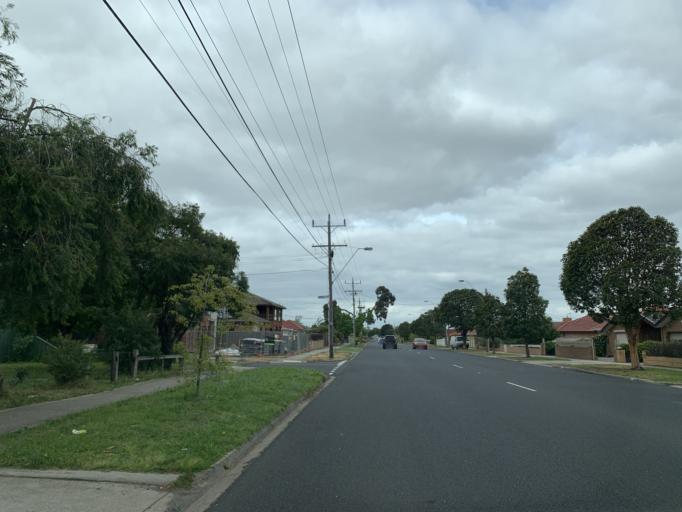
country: AU
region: Victoria
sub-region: Brimbank
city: St Albans
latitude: -37.7458
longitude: 144.8130
